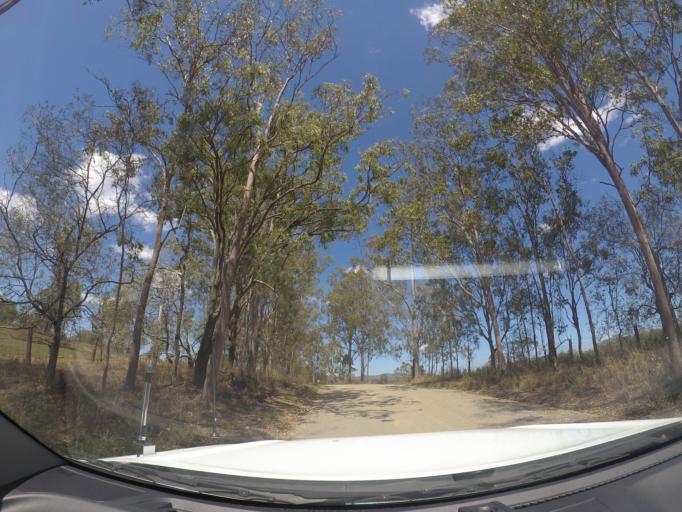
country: AU
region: Queensland
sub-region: Logan
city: Cedar Vale
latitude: -27.8473
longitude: 152.8971
